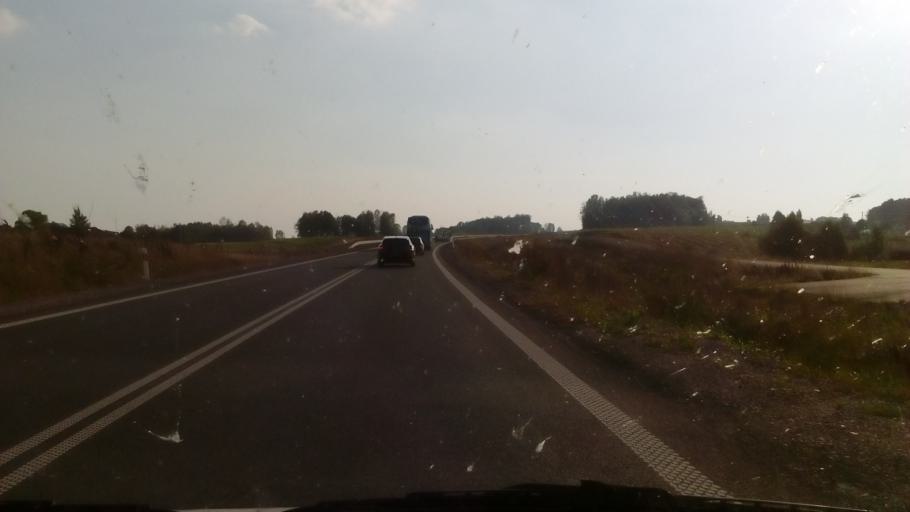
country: PL
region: Podlasie
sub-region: Powiat grajewski
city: Rajgrod
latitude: 53.7631
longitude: 22.8280
